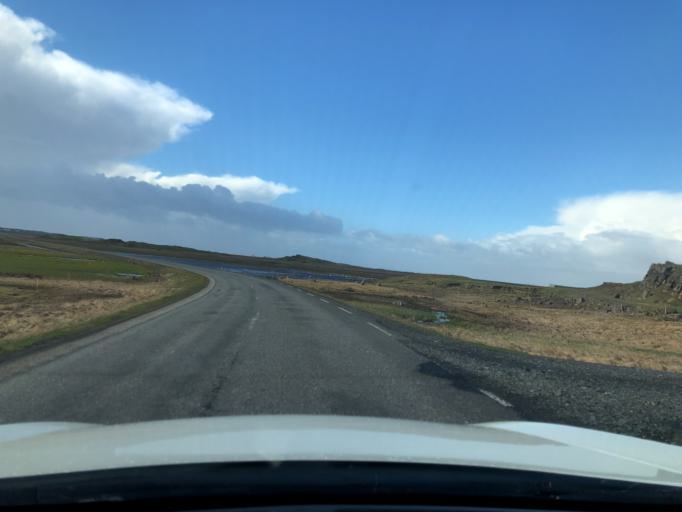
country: IS
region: East
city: Hoefn
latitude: 64.3285
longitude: -15.4168
